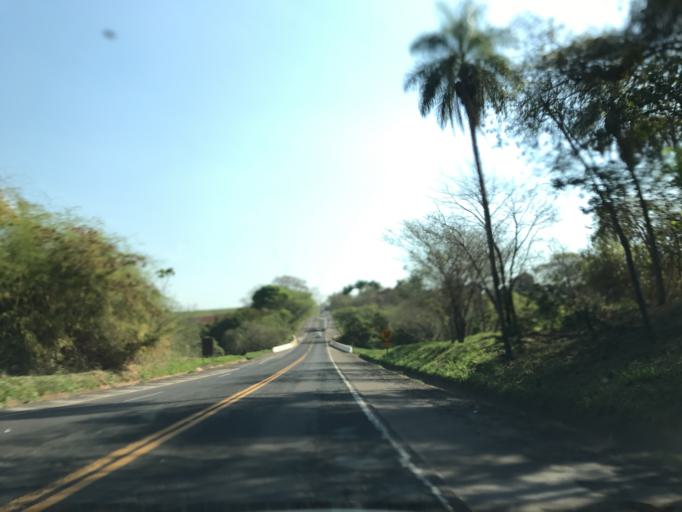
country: BR
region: Sao Paulo
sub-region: Penapolis
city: Penapolis
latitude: -21.4580
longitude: -50.1706
